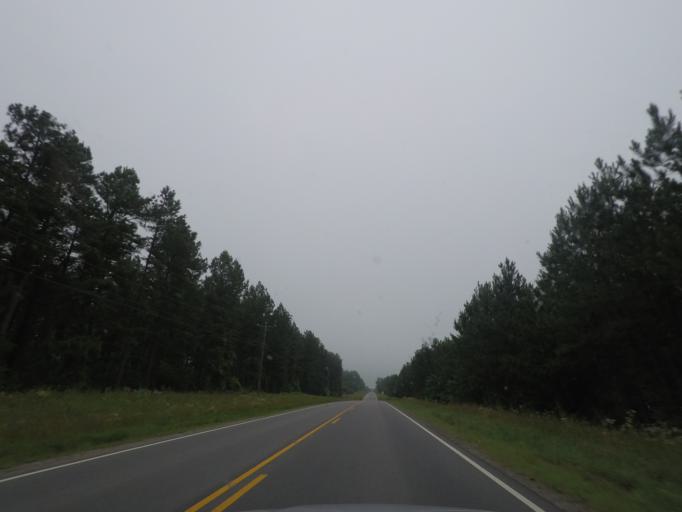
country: US
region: Virginia
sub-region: Buckingham County
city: Buckingham
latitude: 37.5997
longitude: -78.3942
